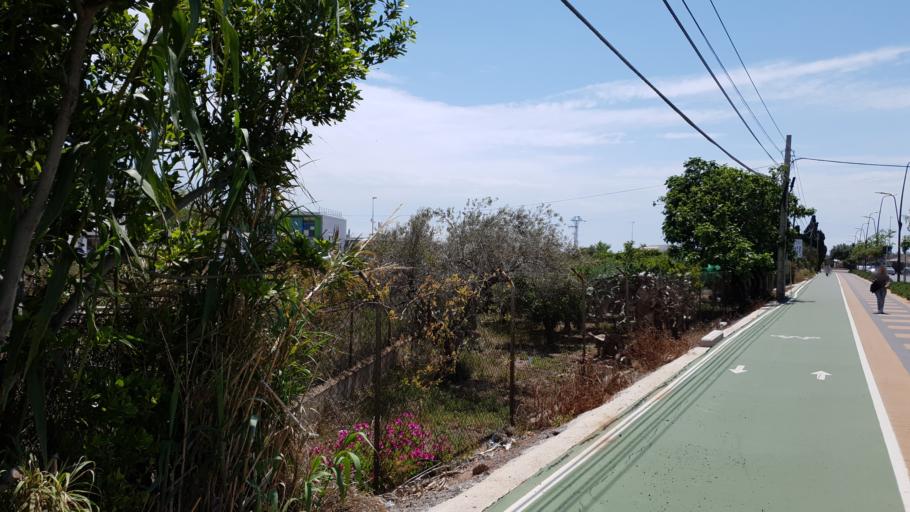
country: ES
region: Valencia
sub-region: Provincia de Castello
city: Burriana
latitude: 39.8798
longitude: -0.0789
